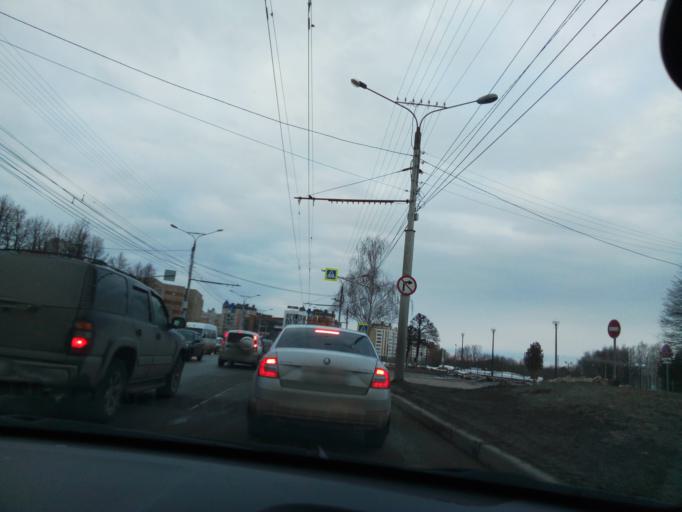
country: RU
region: Chuvashia
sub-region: Cheboksarskiy Rayon
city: Cheboksary
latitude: 56.1465
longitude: 47.2032
